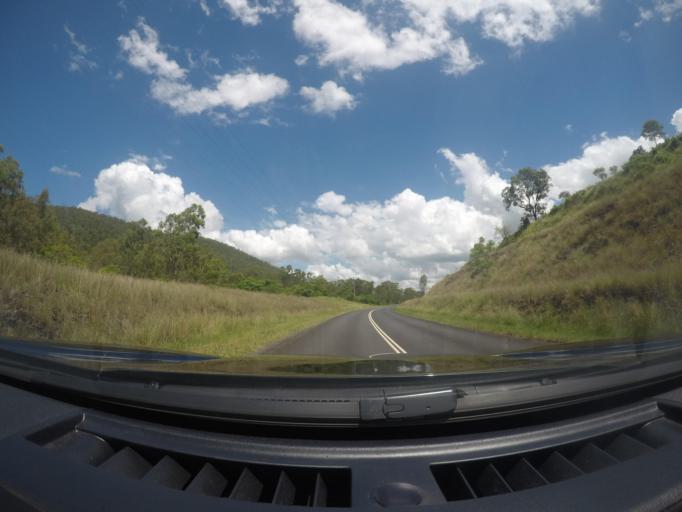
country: AU
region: Queensland
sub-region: Moreton Bay
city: Woodford
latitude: -27.1276
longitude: 152.5523
